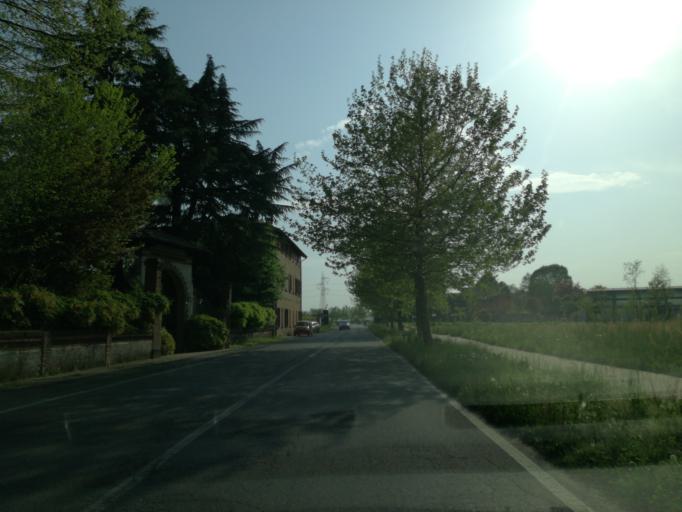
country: IT
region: Lombardy
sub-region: Provincia di Monza e Brianza
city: Porto d'Adda
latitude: 45.6597
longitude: 9.4751
